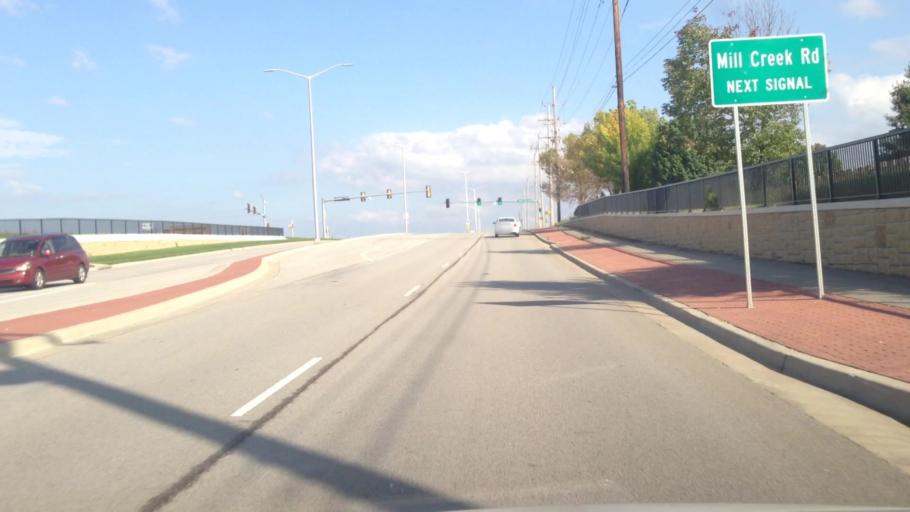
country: US
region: Kansas
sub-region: Johnson County
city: Olathe
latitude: 38.9272
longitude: -94.7903
